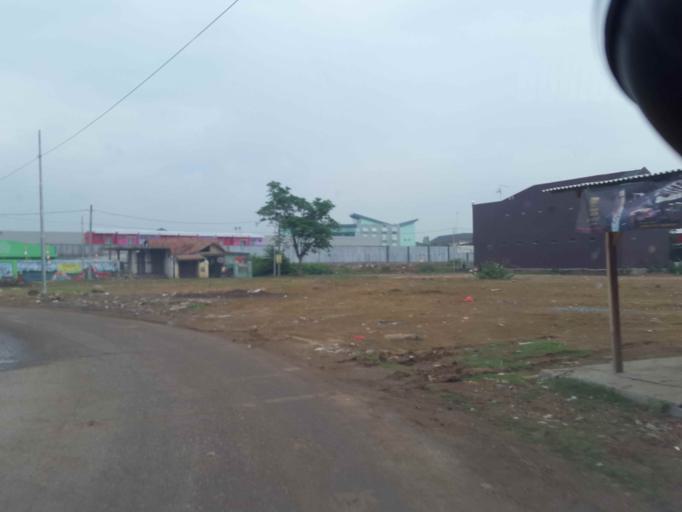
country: ID
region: West Java
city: Cikarang
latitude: -6.2819
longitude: 107.1787
